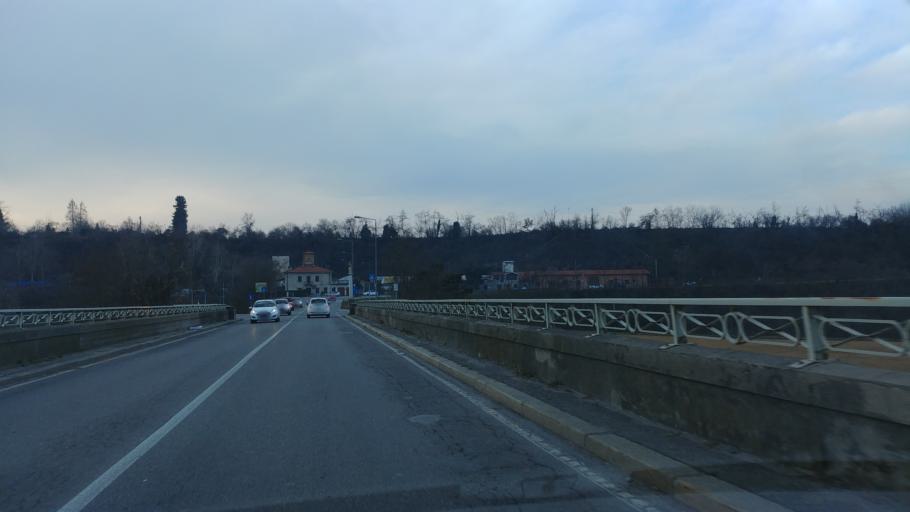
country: IT
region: Piedmont
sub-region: Provincia di Cuneo
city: Cuneo
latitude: 44.3988
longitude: 7.5456
